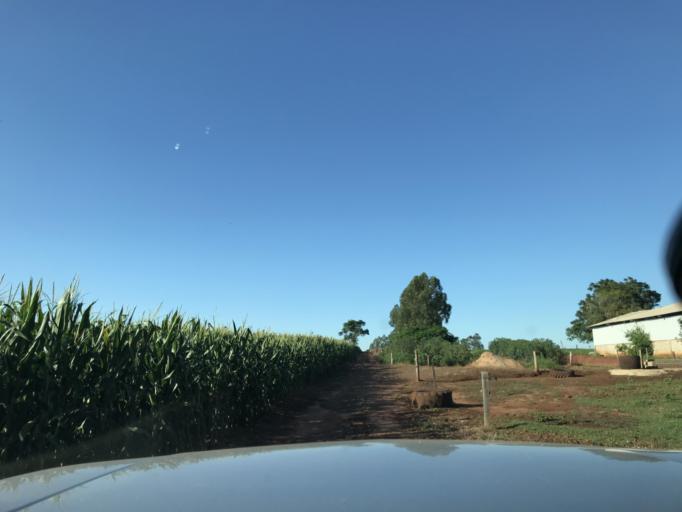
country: BR
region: Parana
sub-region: Palotina
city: Palotina
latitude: -24.2106
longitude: -53.7583
